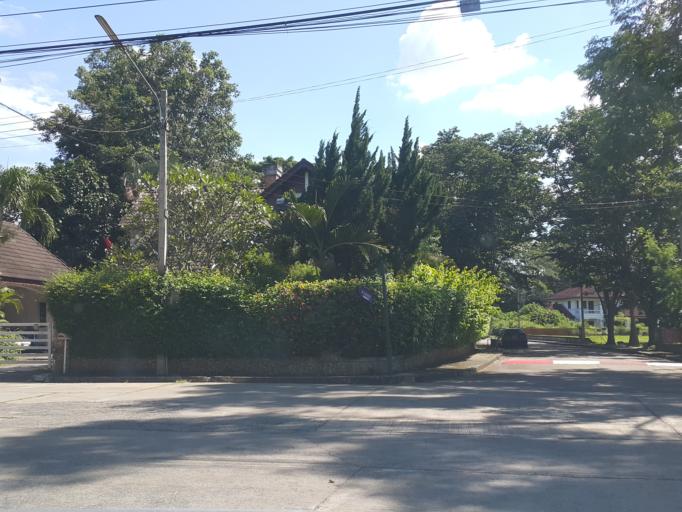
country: TH
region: Chiang Mai
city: San Sai
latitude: 18.8479
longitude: 99.0052
